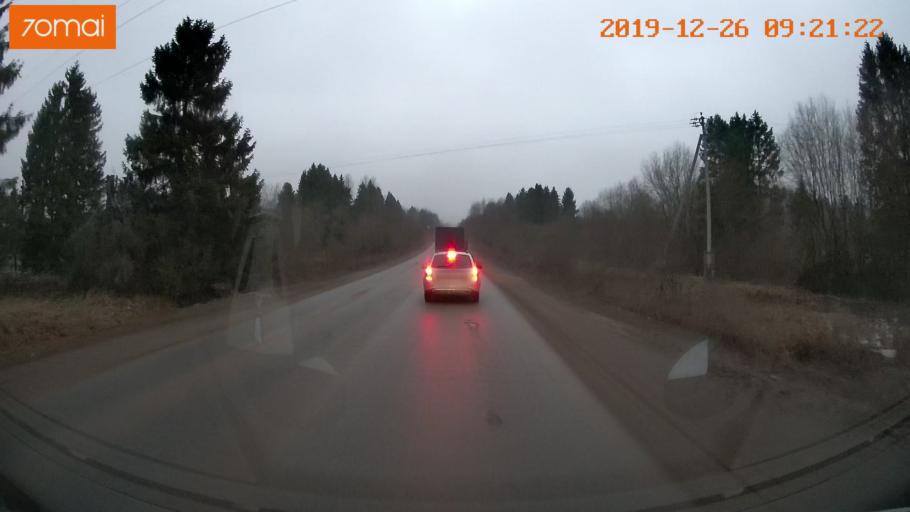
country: RU
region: Vologda
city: Gryazovets
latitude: 58.9699
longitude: 40.2247
